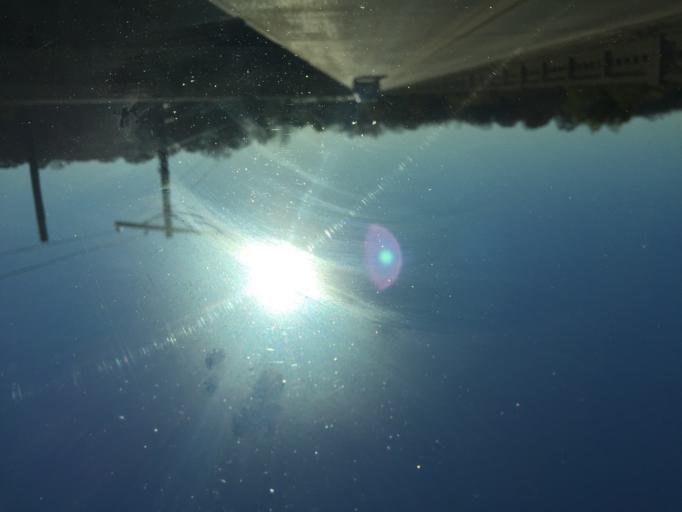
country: US
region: Mississippi
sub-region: Hinds County
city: Jackson
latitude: 32.2894
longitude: -90.1786
